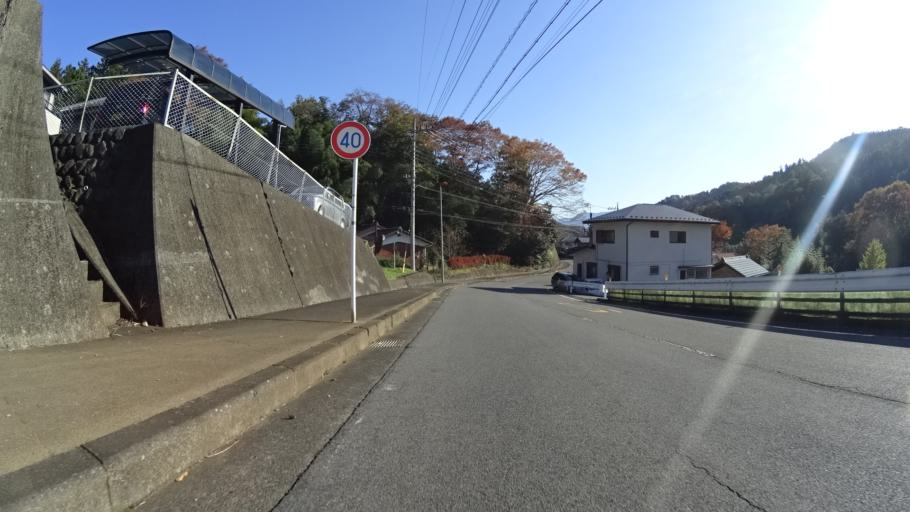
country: JP
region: Yamanashi
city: Uenohara
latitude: 35.6497
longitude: 139.1219
